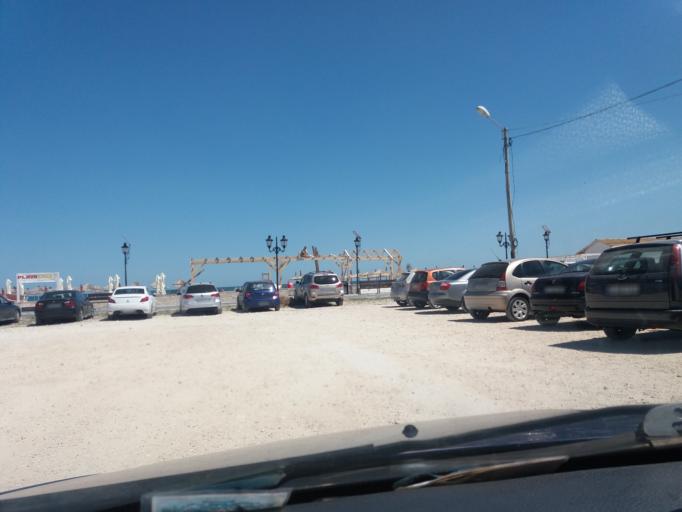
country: RO
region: Constanta
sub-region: Comuna Navodari
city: Navodari
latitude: 44.3195
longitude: 28.6347
